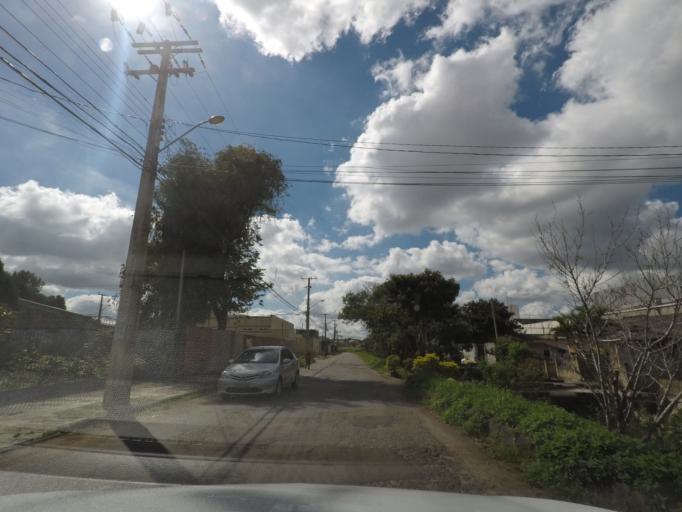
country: BR
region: Parana
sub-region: Sao Jose Dos Pinhais
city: Sao Jose dos Pinhais
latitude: -25.4987
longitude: -49.2259
